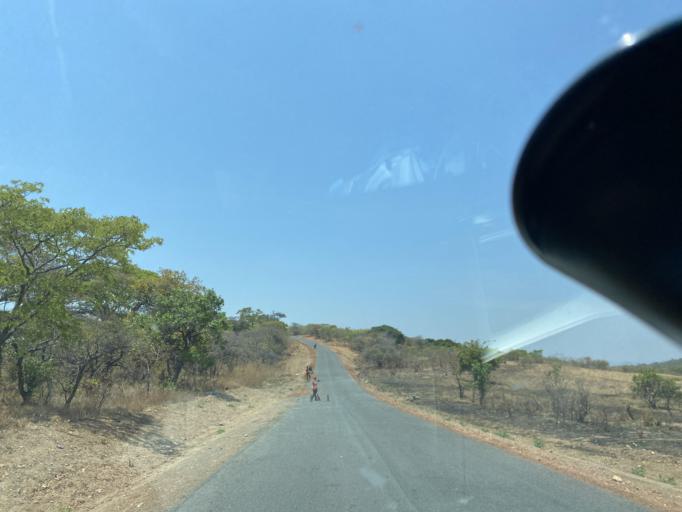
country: ZM
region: Lusaka
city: Kafue
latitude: -15.8413
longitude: 28.4090
